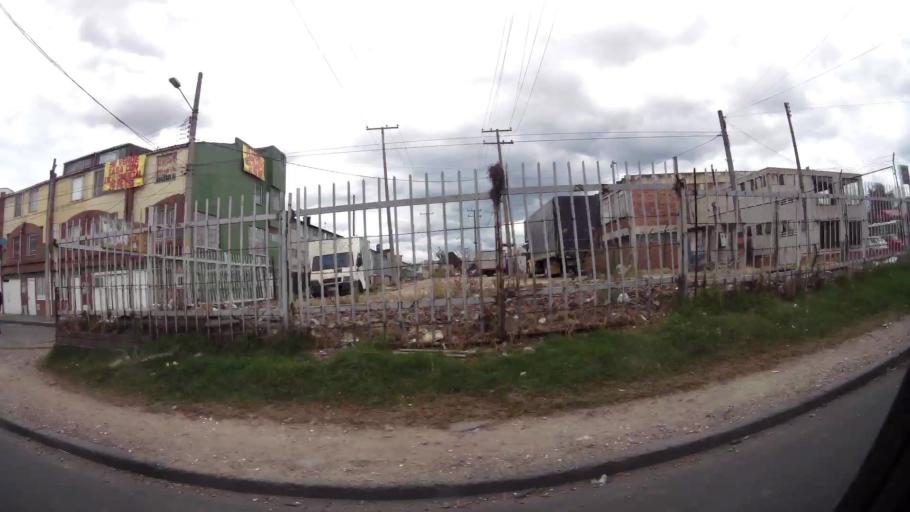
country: CO
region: Cundinamarca
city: Funza
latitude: 4.7162
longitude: -74.1185
